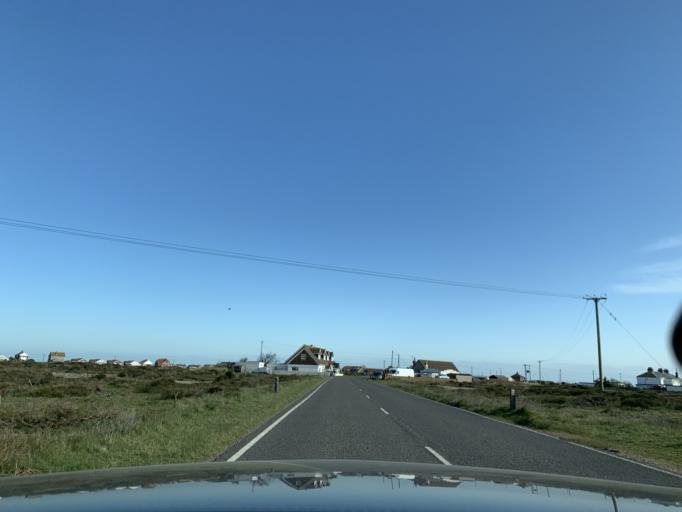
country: GB
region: England
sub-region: Kent
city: New Romney
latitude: 50.9303
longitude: 0.9674
